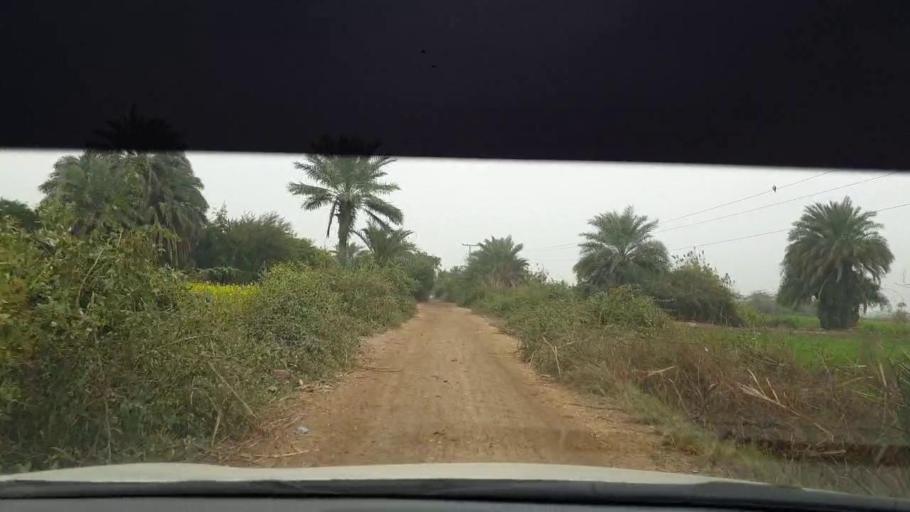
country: PK
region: Sindh
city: Berani
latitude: 25.7798
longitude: 68.7896
